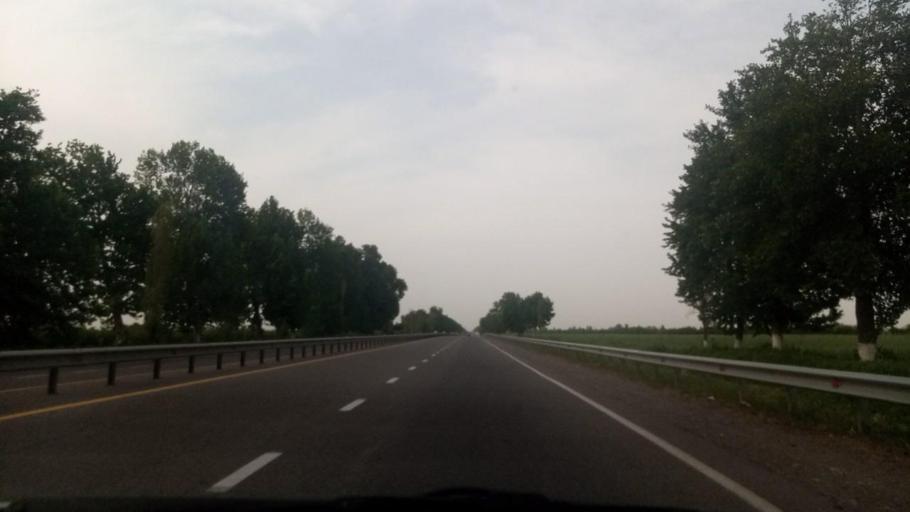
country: UZ
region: Toshkent Shahri
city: Bektemir
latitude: 41.1938
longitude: 69.4032
